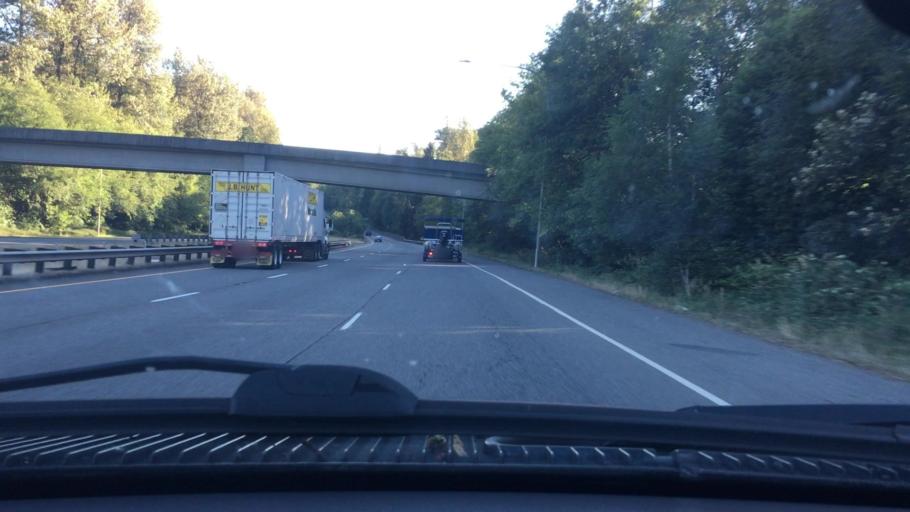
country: US
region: Washington
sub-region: Mason County
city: Shelton
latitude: 47.2210
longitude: -123.0774
